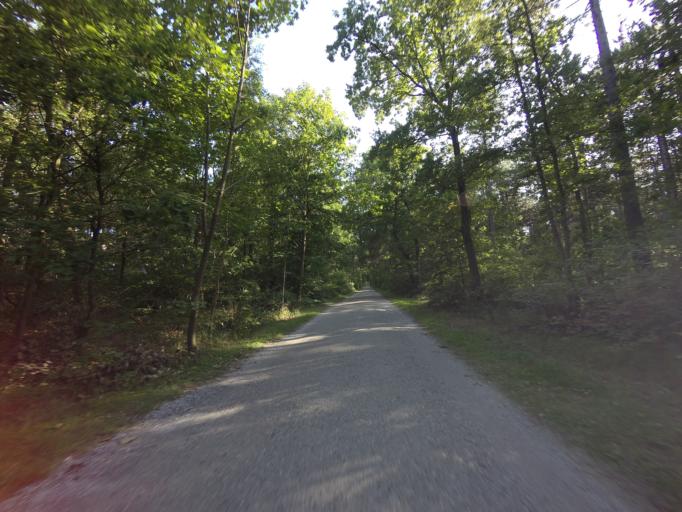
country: NL
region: Friesland
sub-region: Gemeente Terschelling
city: West-Terschelling
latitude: 53.3759
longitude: 5.2182
